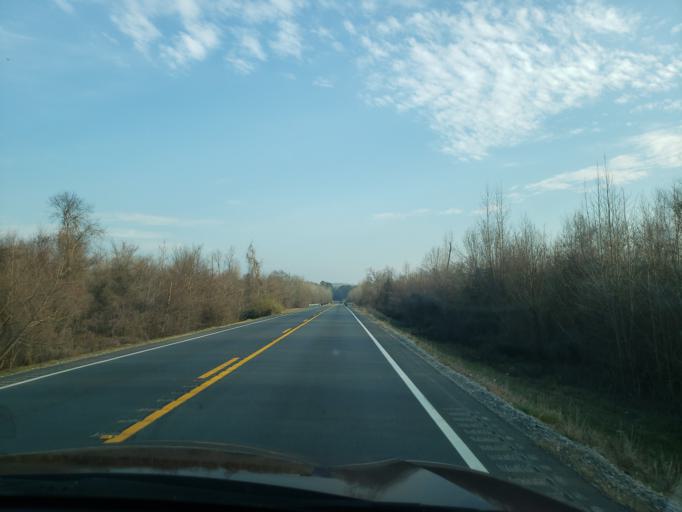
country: US
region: Alabama
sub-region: Hale County
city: Greensboro
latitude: 32.8315
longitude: -87.6051
